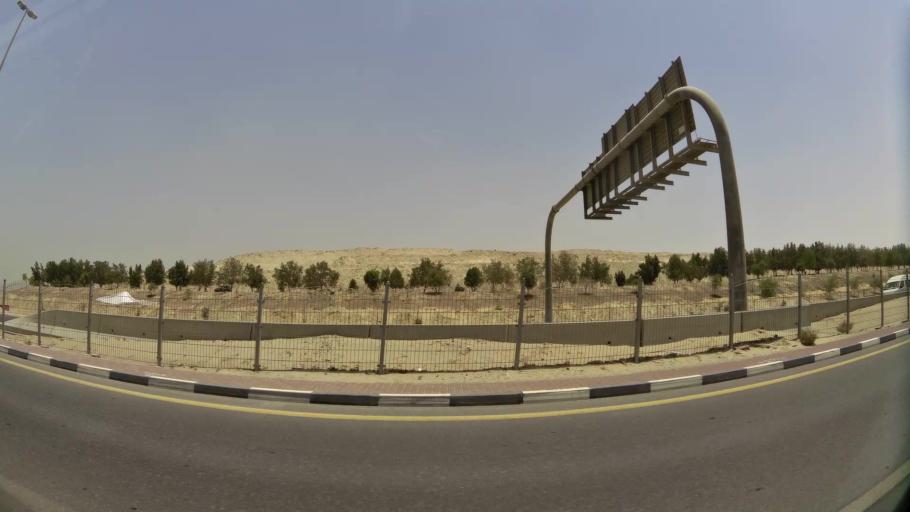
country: AE
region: Ash Shariqah
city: Sharjah
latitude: 25.2766
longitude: 55.4266
